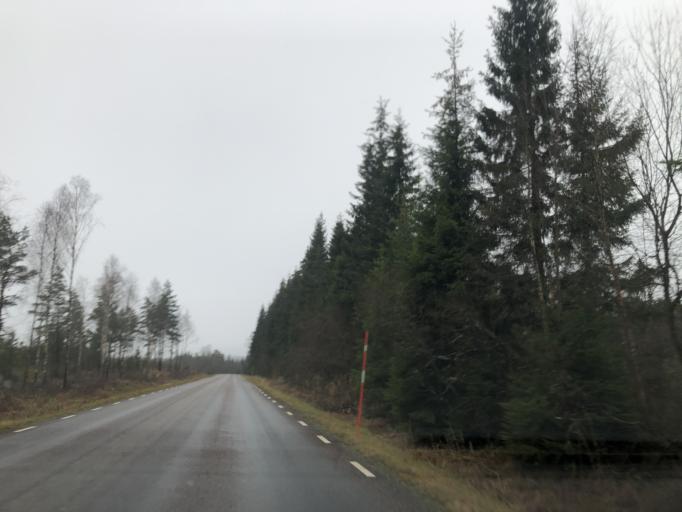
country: SE
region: Vaestra Goetaland
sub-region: Ulricehamns Kommun
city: Ulricehamn
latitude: 57.7085
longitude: 13.5713
